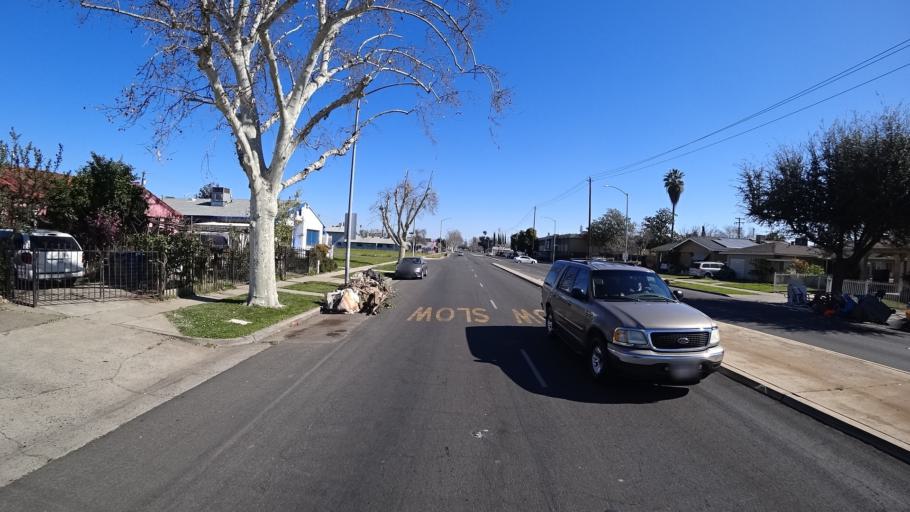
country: US
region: California
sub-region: Fresno County
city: West Park
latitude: 36.7234
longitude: -119.8100
